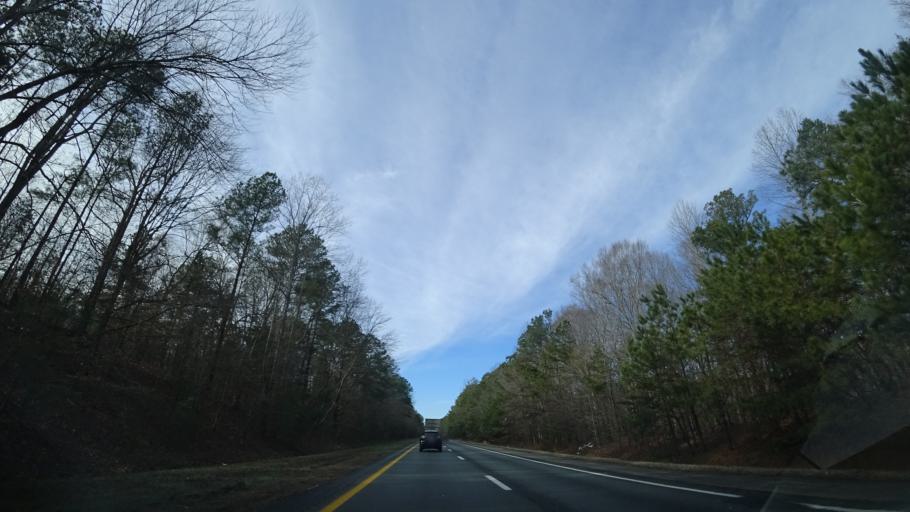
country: US
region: Virginia
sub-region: New Kent County
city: New Kent
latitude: 37.4868
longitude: -76.9695
